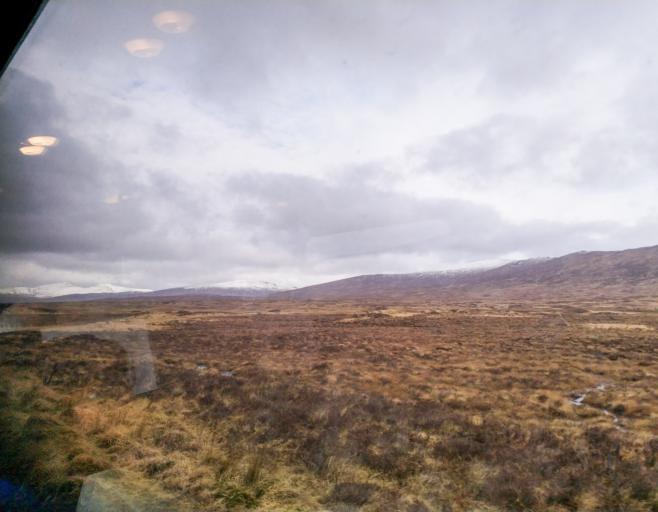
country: GB
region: Scotland
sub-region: Highland
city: Spean Bridge
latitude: 56.7054
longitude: -4.5919
